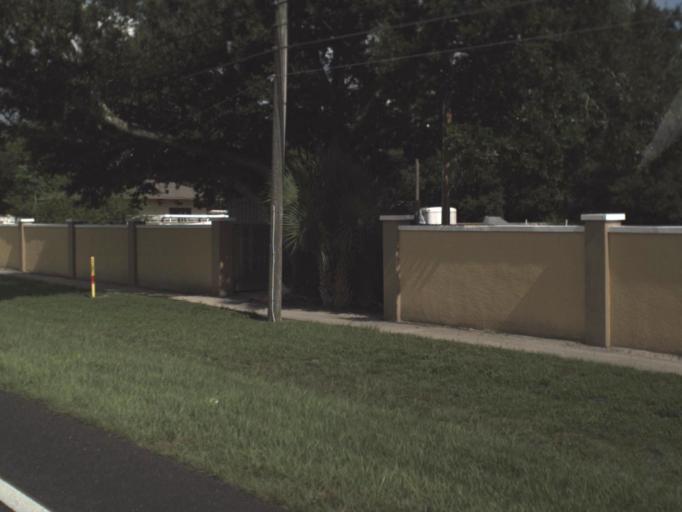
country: US
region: Florida
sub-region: Hillsborough County
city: Temple Terrace
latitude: 28.0545
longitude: -82.3884
